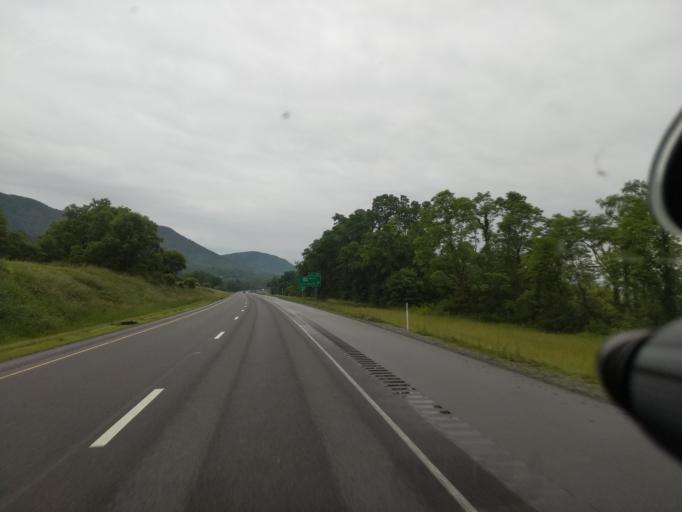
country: US
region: Pennsylvania
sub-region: Clinton County
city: Castanea
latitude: 41.0610
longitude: -77.4307
